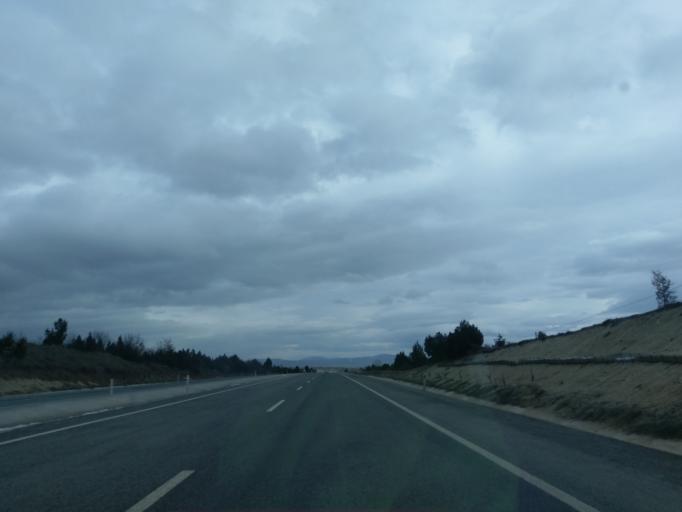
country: TR
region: Kuetahya
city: Aslanapa
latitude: 39.2273
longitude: 29.7604
